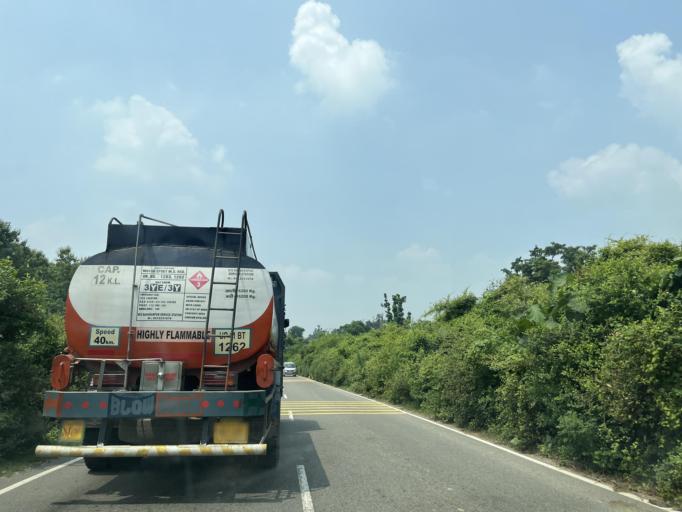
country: IN
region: Uttarakhand
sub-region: Haridwar
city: Haridwar
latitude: 29.8426
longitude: 78.1908
